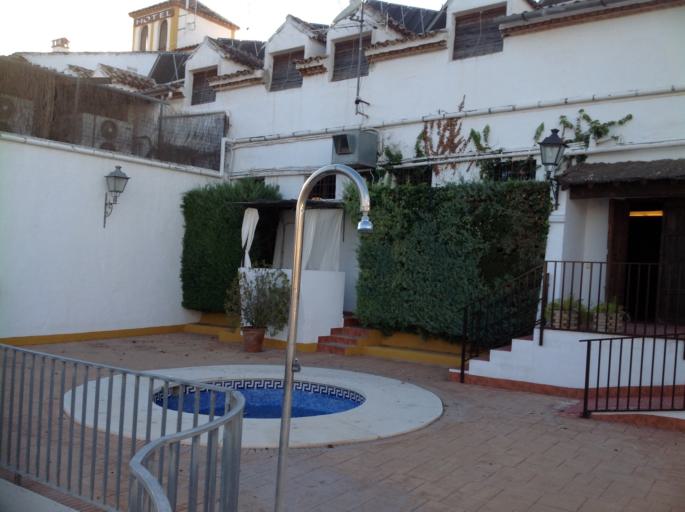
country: ES
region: Andalusia
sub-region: Provincia de Malaga
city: Alameda
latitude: 37.1998
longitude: -4.6409
